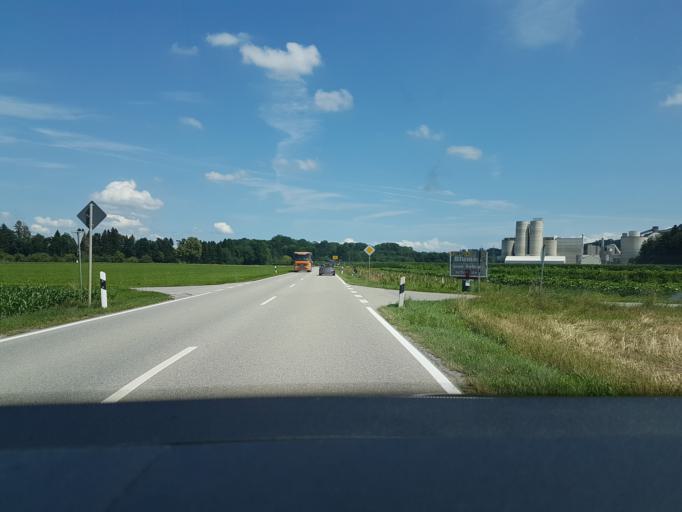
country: DE
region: Bavaria
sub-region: Upper Bavaria
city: Rohrdorf
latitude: 47.7921
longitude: 12.1698
